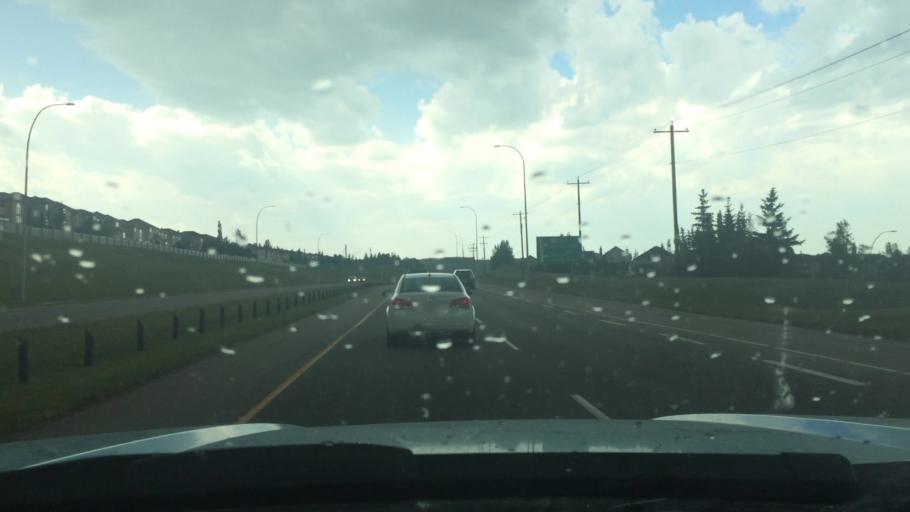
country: CA
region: Alberta
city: Calgary
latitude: 51.1453
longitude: -114.1281
